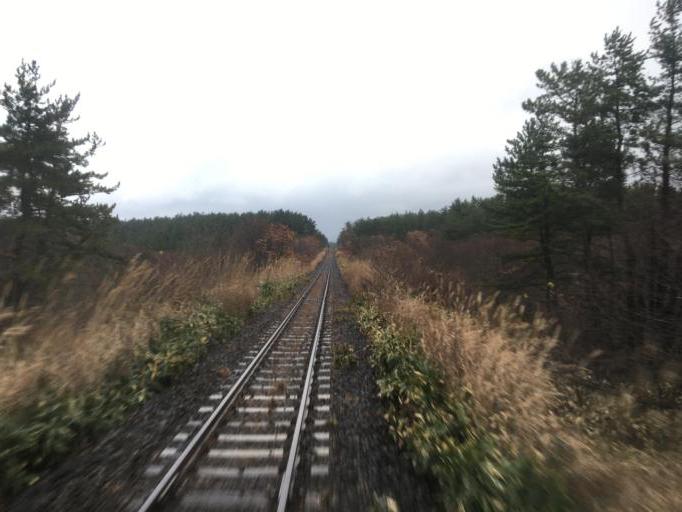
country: JP
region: Aomori
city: Misawa
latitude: 40.9448
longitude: 141.2142
